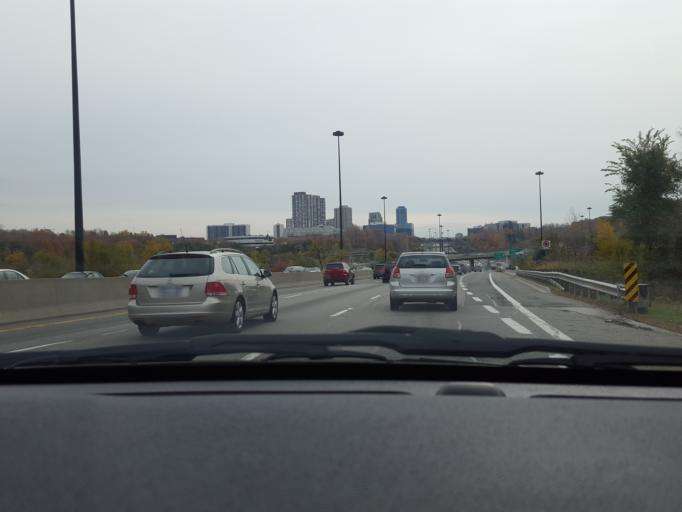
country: CA
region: Ontario
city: Willowdale
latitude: 43.7426
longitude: -79.3325
